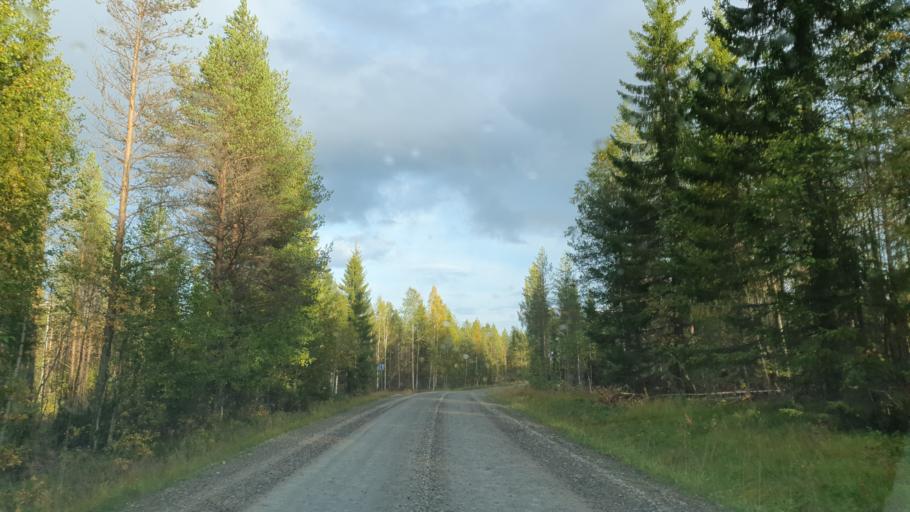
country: FI
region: Kainuu
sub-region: Kehys-Kainuu
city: Kuhmo
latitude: 64.4221
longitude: 29.3599
